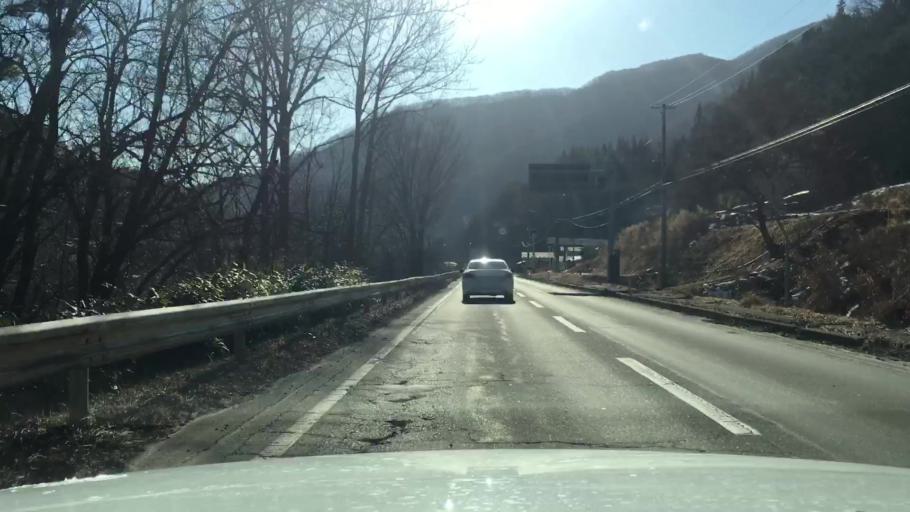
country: JP
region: Iwate
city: Tono
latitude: 39.6184
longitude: 141.6233
